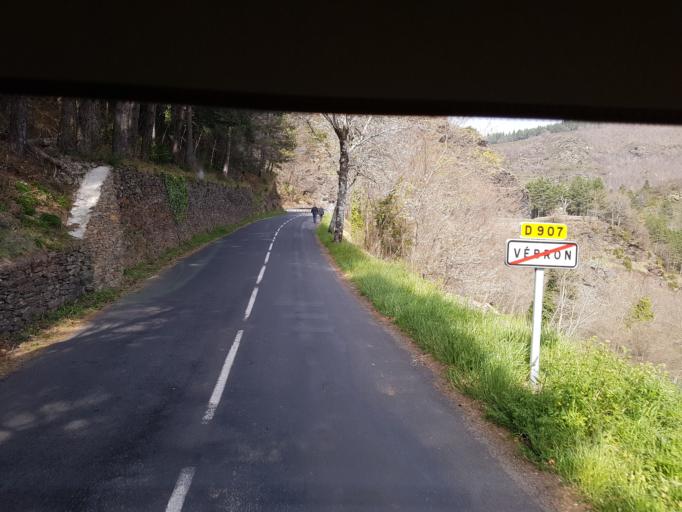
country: FR
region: Languedoc-Roussillon
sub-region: Departement de la Lozere
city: Florac
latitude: 44.2417
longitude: 3.5793
